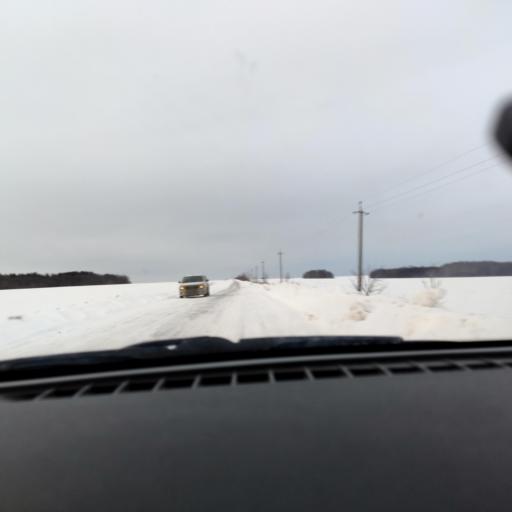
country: RU
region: Bashkortostan
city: Iglino
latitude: 54.7412
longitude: 56.5371
